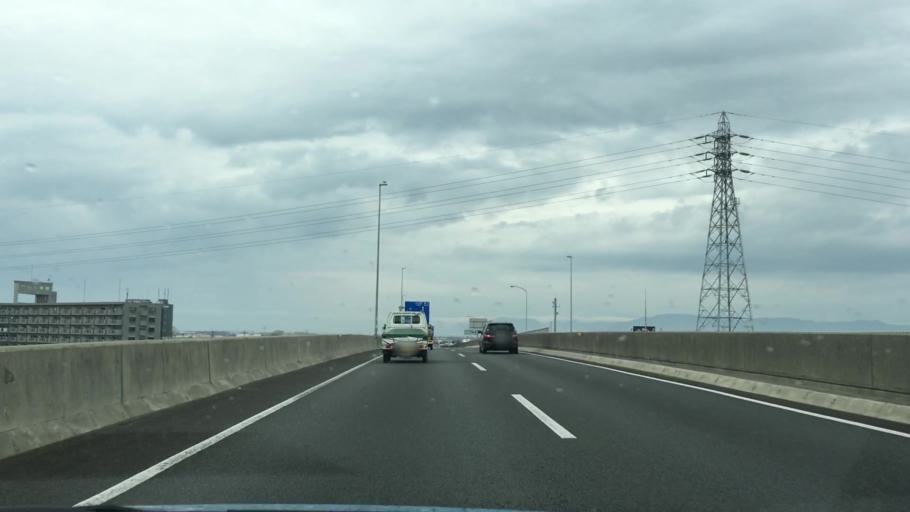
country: JP
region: Aichi
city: Toyohashi
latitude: 34.7332
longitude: 137.3504
